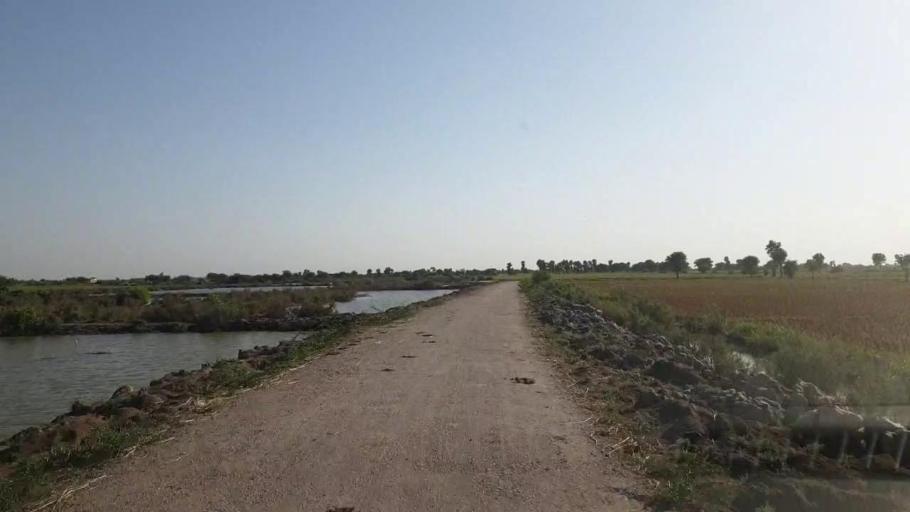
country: PK
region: Sindh
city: Badin
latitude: 24.5963
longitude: 68.9112
